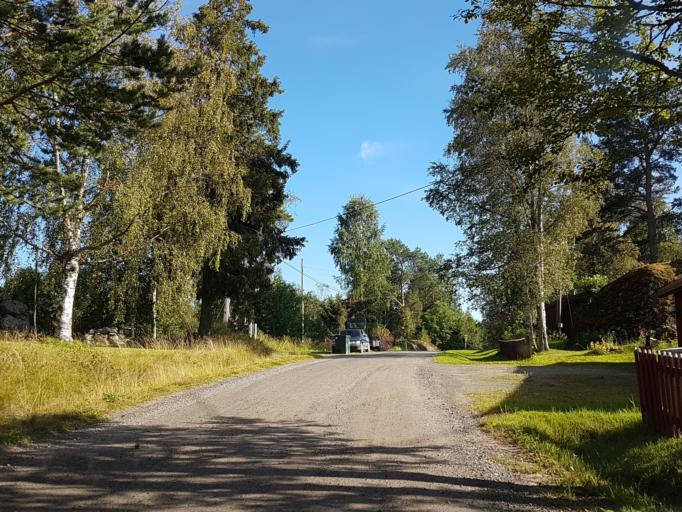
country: SE
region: Vaesterbotten
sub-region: Robertsfors Kommun
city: Robertsfors
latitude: 64.0619
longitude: 20.8654
